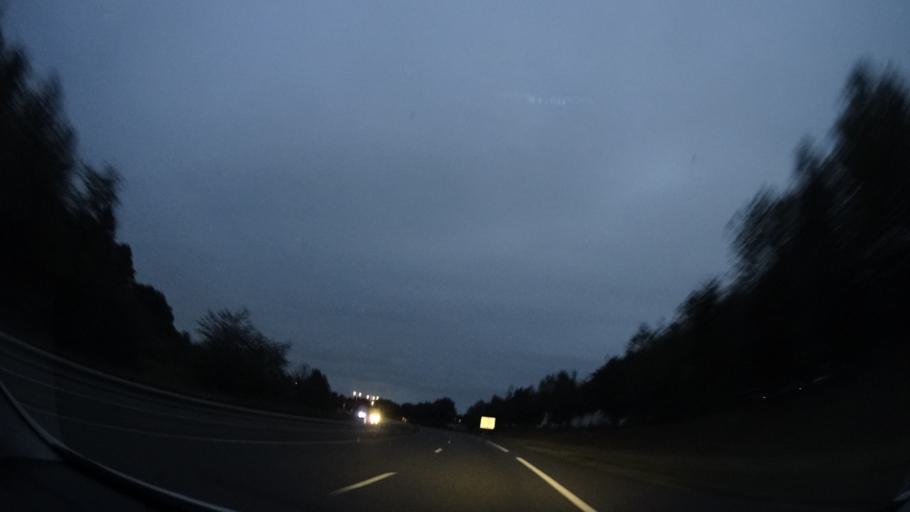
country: FR
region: Pays de la Loire
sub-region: Departement de la Mayenne
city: Saint-Berthevin
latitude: 48.0739
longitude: -0.8462
